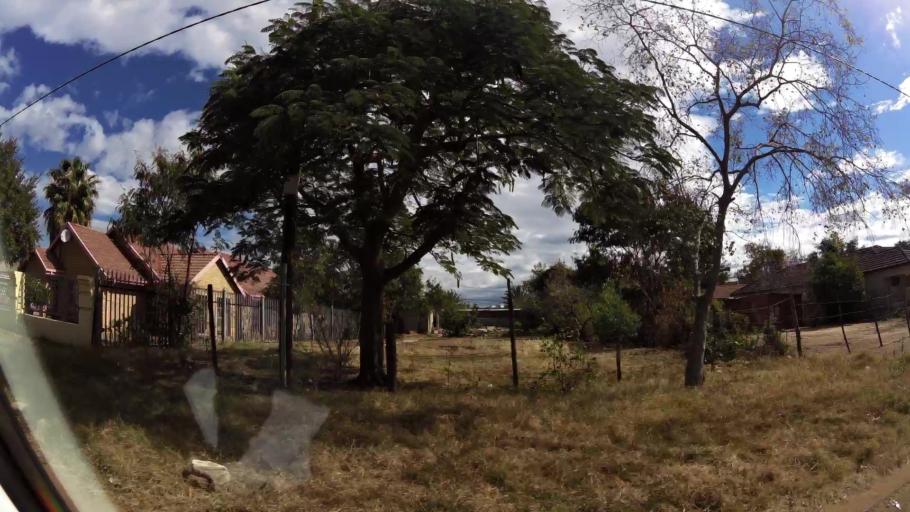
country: ZA
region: Limpopo
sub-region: Waterberg District Municipality
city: Bela-Bela
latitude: -24.8892
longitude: 28.3061
